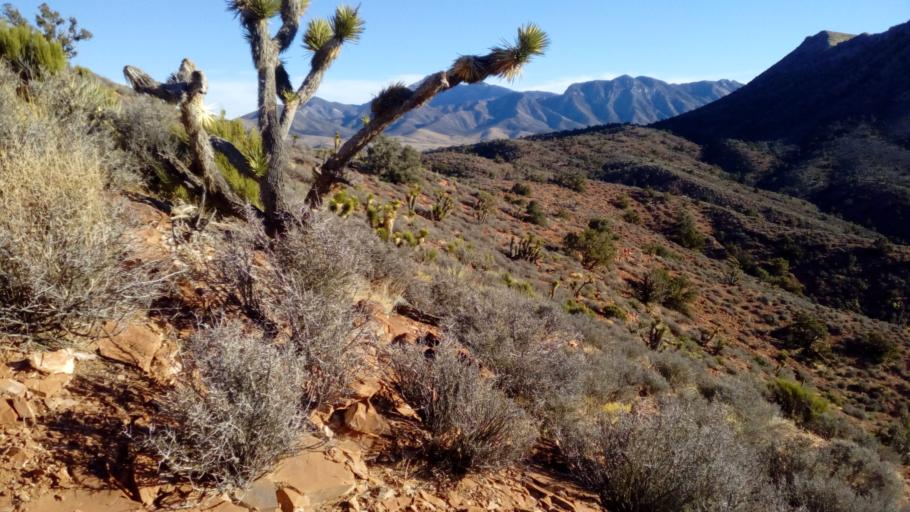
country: US
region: Nevada
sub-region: Clark County
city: Summerlin South
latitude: 36.0634
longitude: -115.5714
